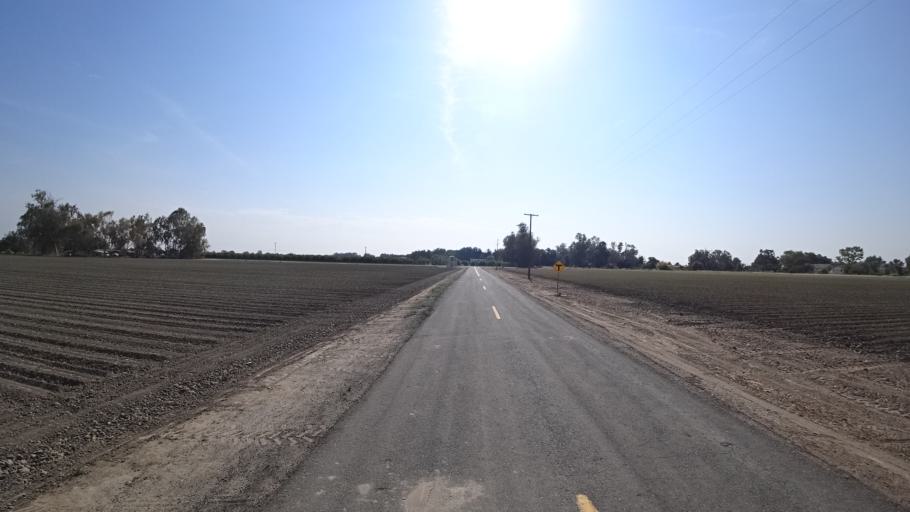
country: US
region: California
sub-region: Kings County
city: Lemoore
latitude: 36.3367
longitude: -119.8535
